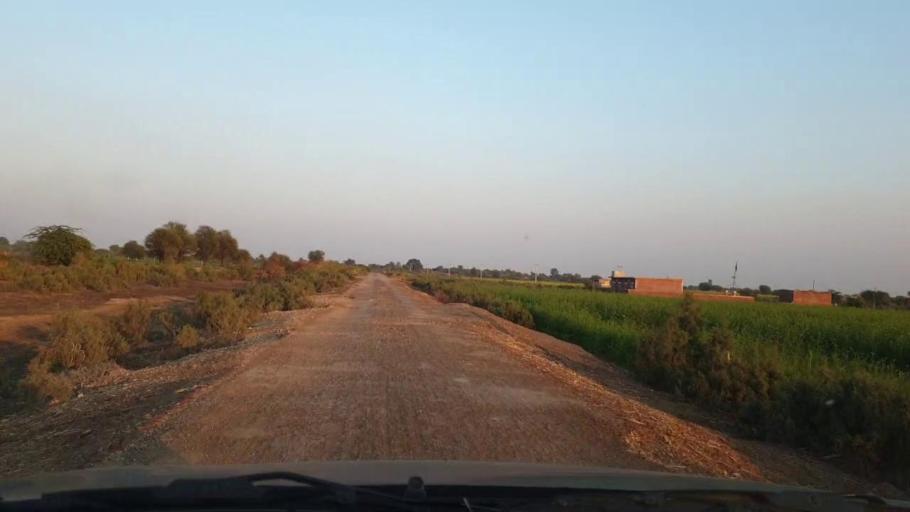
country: PK
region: Sindh
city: Jhol
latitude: 25.9209
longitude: 68.9547
